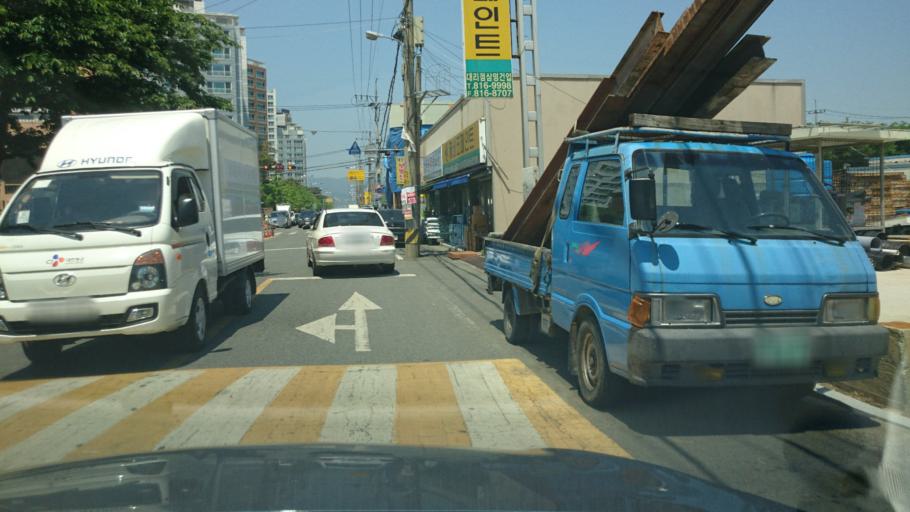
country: KR
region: Gyeongsangbuk-do
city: Gyeongsan-si
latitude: 35.8296
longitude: 128.7388
